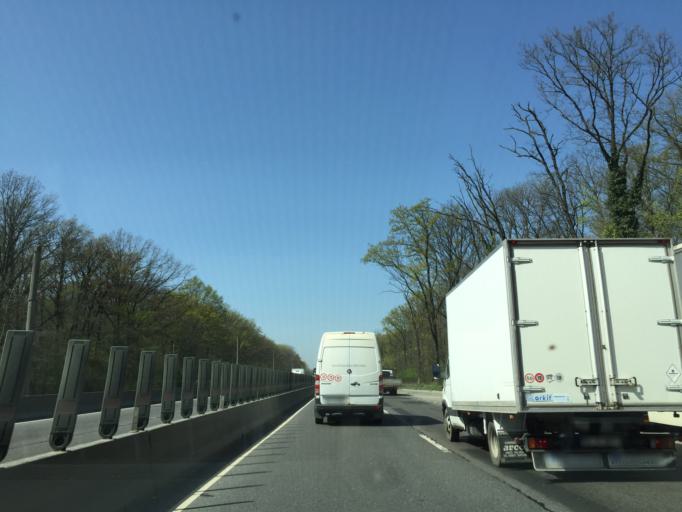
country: RO
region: Ilfov
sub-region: Comuna Tunari
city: Tunari
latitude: 44.5394
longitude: 26.1127
